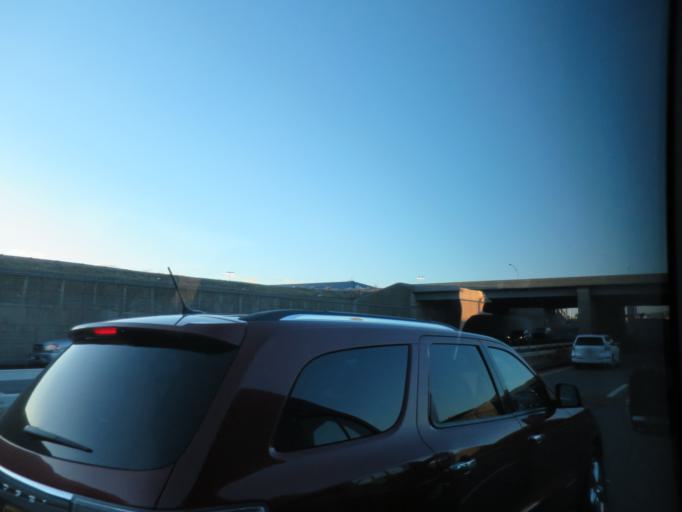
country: US
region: New York
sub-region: Queens County
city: Jamaica
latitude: 40.6525
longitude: -73.7863
